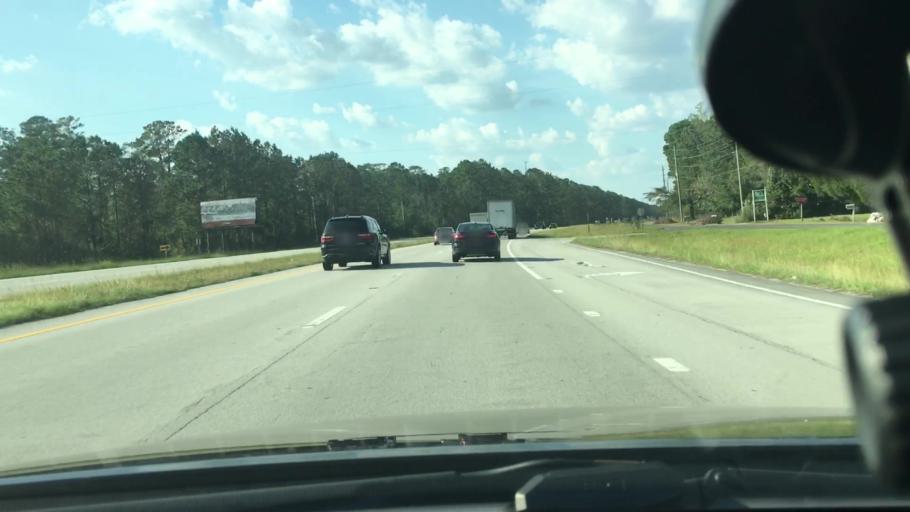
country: US
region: North Carolina
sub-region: Craven County
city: Neuse Forest
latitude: 34.9722
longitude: -76.9725
